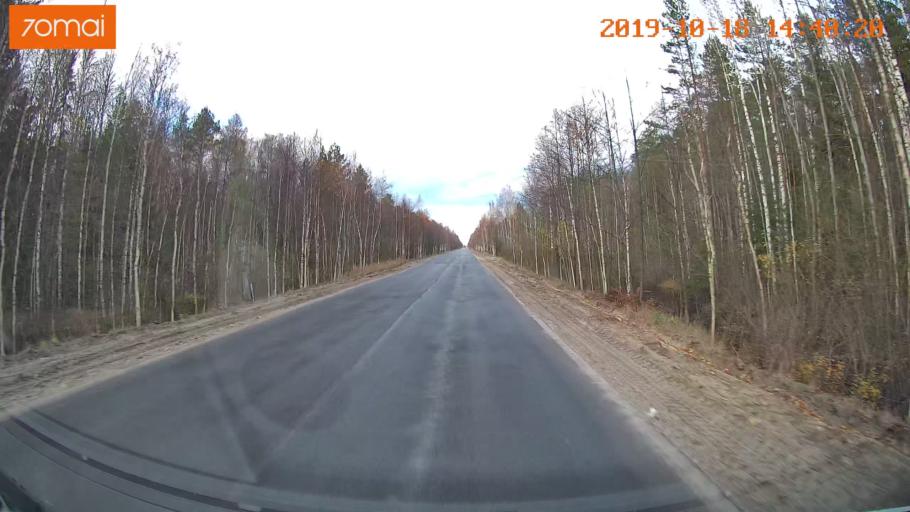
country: RU
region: Vladimir
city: Velikodvorskiy
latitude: 55.2751
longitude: 40.6688
